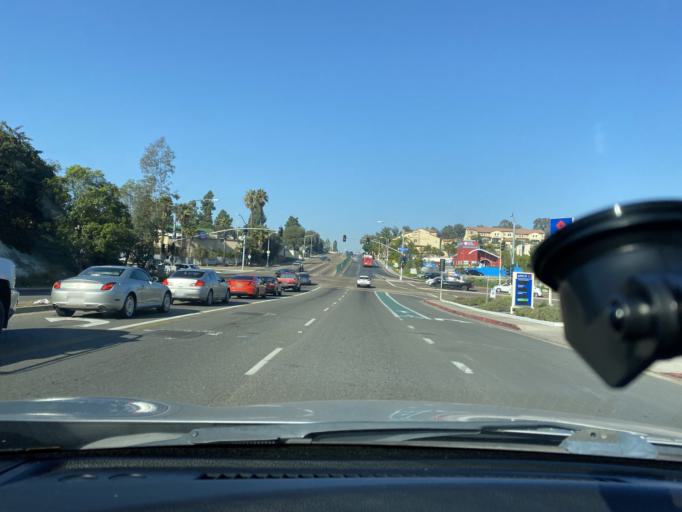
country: US
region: California
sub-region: San Diego County
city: Lemon Grove
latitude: 32.7481
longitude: -117.0795
